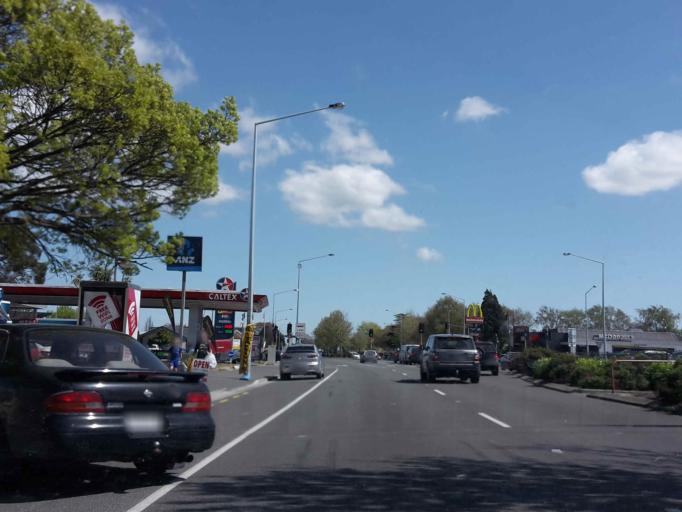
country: NZ
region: Canterbury
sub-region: Selwyn District
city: Prebbleton
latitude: -43.5436
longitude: 172.5238
